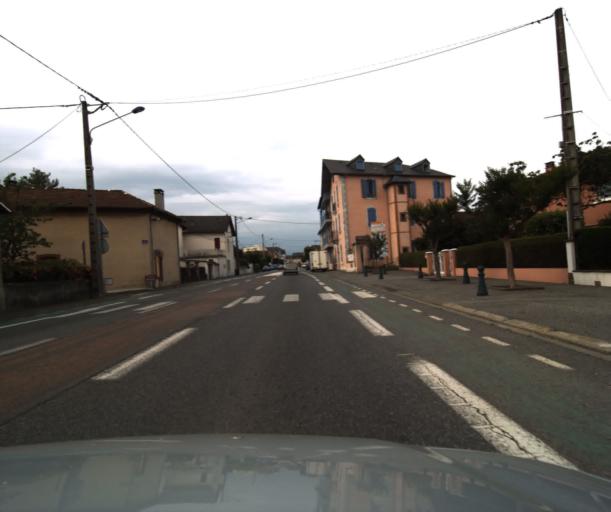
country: FR
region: Midi-Pyrenees
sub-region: Departement des Hautes-Pyrenees
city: Aureilhan
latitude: 43.2361
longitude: 0.0930
